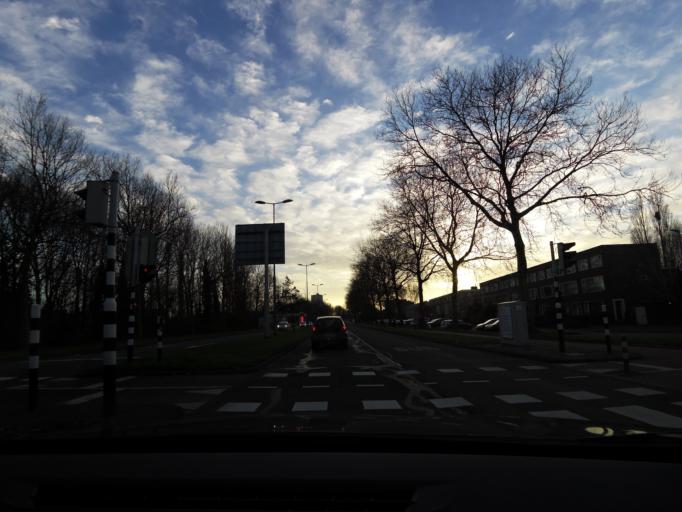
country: NL
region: South Holland
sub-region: Gemeente Spijkenisse
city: Spijkenisse
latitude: 51.8728
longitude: 4.3572
